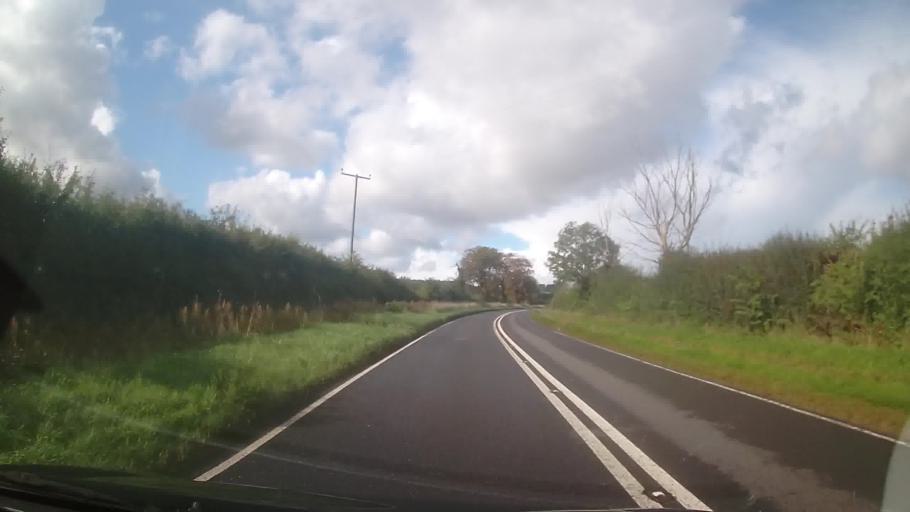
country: GB
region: England
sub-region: Gloucestershire
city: Moreton in Marsh
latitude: 51.9888
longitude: -1.7242
